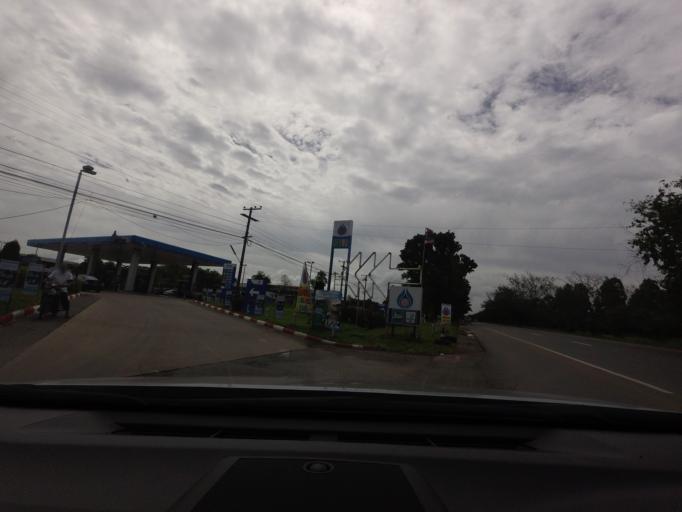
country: TH
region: Chumphon
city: Lamae
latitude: 9.7338
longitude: 99.1023
